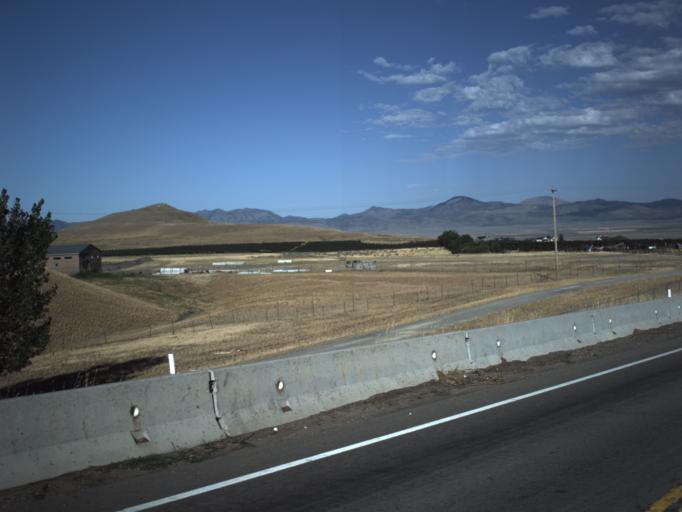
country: US
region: Utah
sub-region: Utah County
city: Santaquin
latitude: 39.9816
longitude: -111.8058
